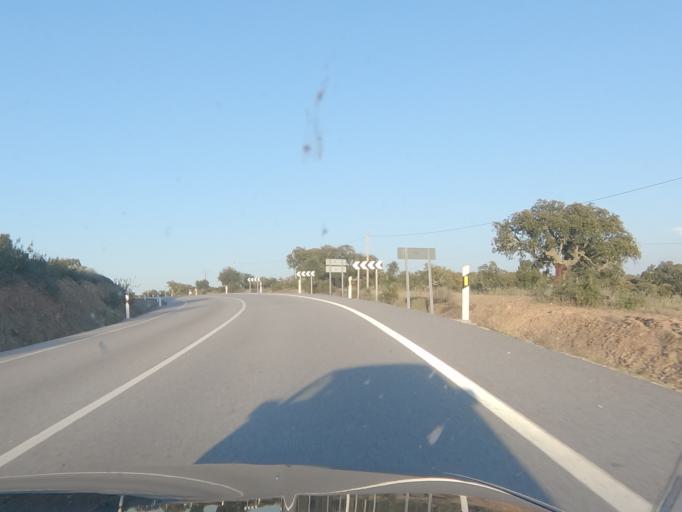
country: ES
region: Extremadura
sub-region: Provincia de Caceres
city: Carbajo
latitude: 39.5047
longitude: -7.1580
